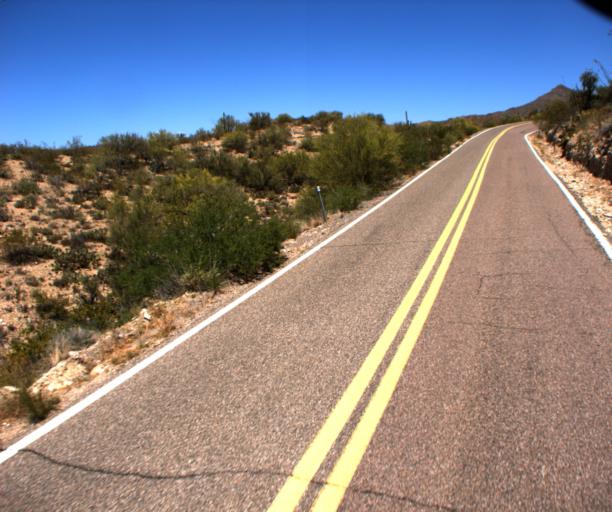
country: US
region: Arizona
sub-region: Yavapai County
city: Bagdad
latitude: 34.4615
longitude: -113.0093
